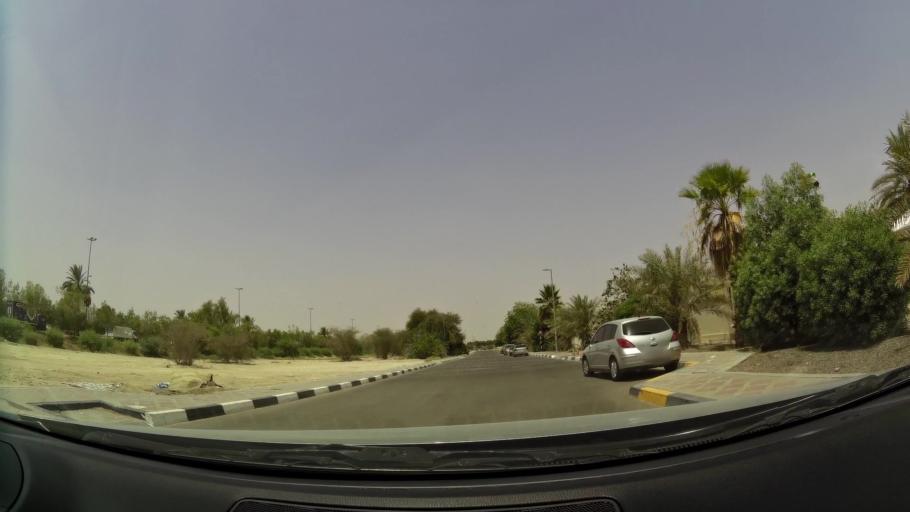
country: AE
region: Abu Dhabi
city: Al Ain
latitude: 24.1842
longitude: 55.7398
